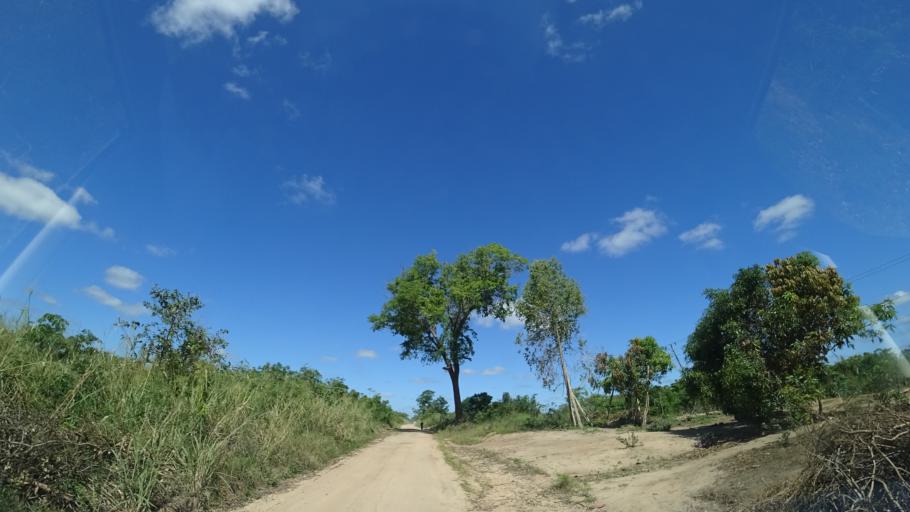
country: MZ
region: Sofala
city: Dondo
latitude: -19.3210
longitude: 34.6915
